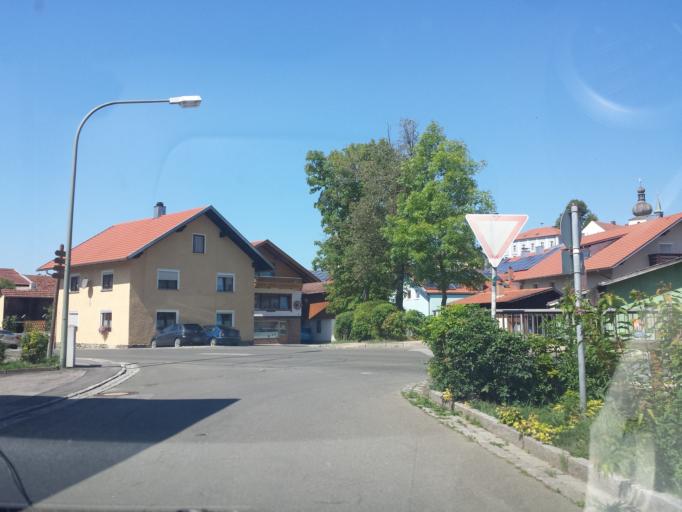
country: DE
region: Bavaria
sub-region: Upper Palatinate
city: Neukirchen
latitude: 49.2564
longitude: 12.9718
